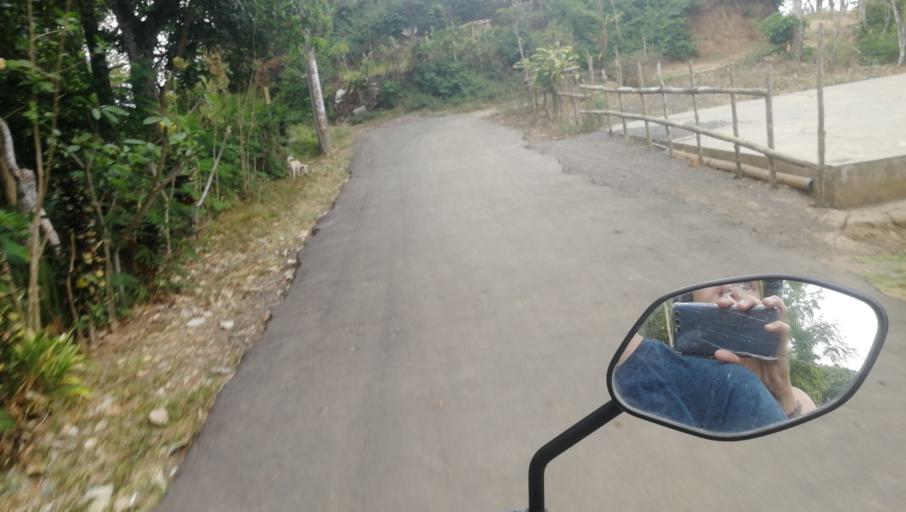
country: ID
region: Bali
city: Banjar Ambengan
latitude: -8.2084
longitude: 115.1104
